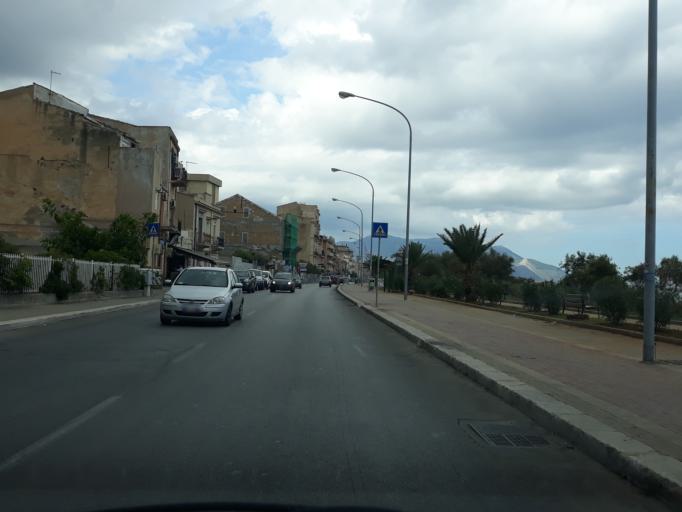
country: IT
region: Sicily
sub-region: Palermo
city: Ciaculli
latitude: 38.1029
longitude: 13.3945
